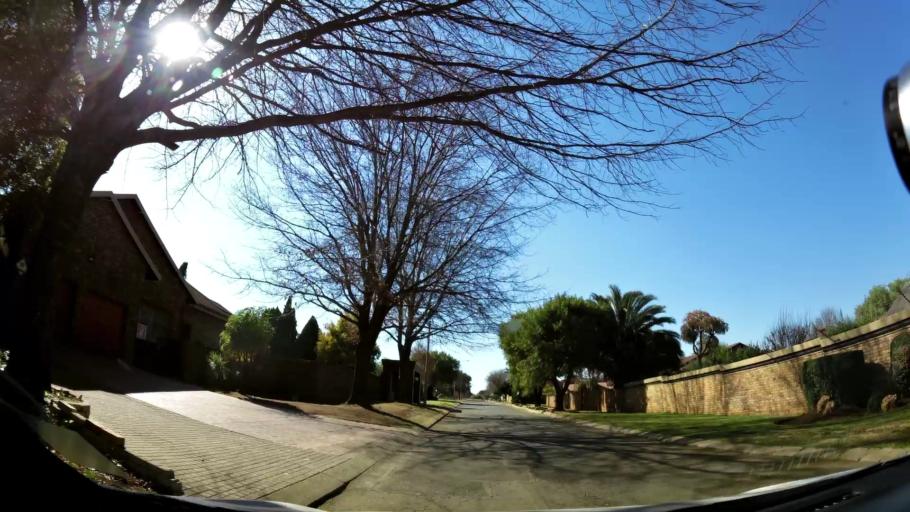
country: ZA
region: Gauteng
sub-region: Ekurhuleni Metropolitan Municipality
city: Germiston
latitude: -26.3001
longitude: 28.0961
